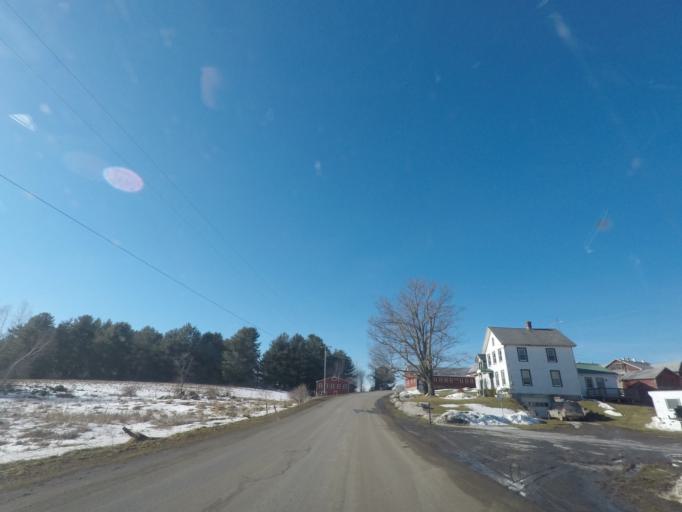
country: US
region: New York
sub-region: Rensselaer County
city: Averill Park
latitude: 42.6296
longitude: -73.5104
